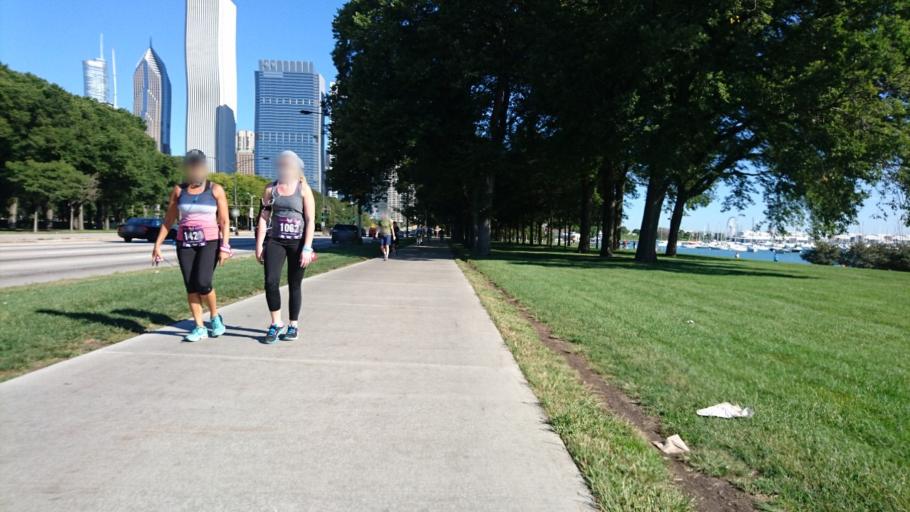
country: US
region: Illinois
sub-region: Cook County
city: Chicago
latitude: 41.8771
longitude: -87.6170
